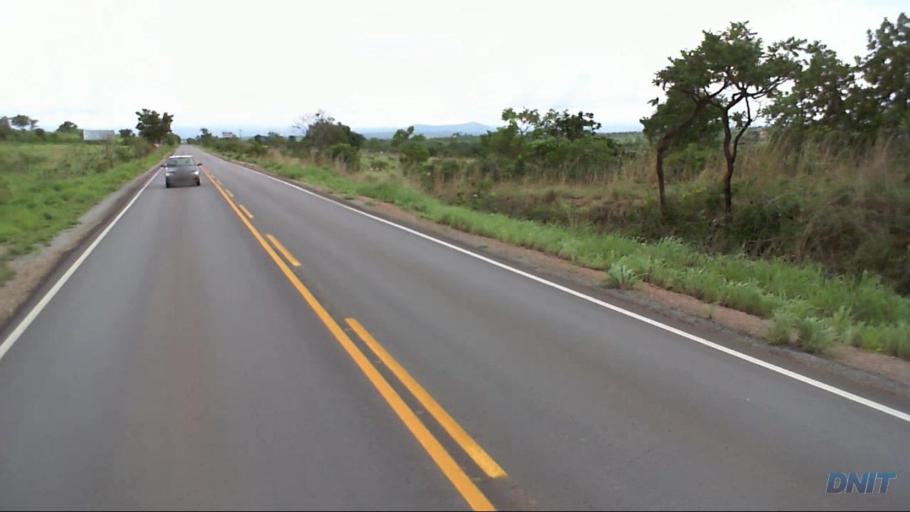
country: BR
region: Goias
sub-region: Padre Bernardo
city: Padre Bernardo
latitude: -15.1962
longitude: -48.2840
